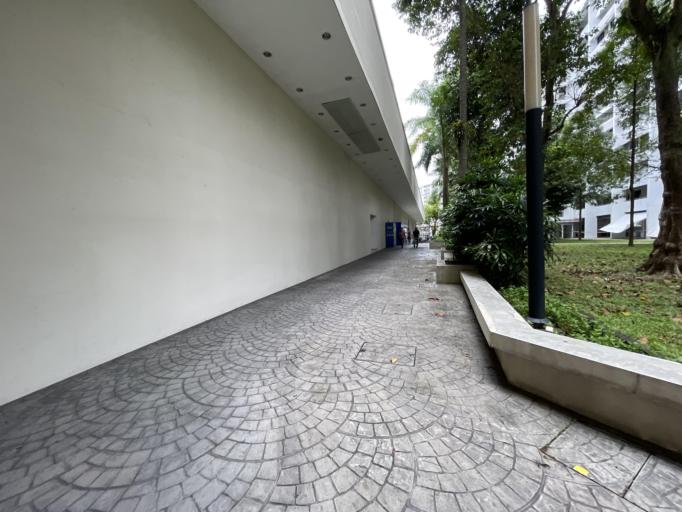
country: SG
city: Singapore
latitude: 1.3041
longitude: 103.7669
